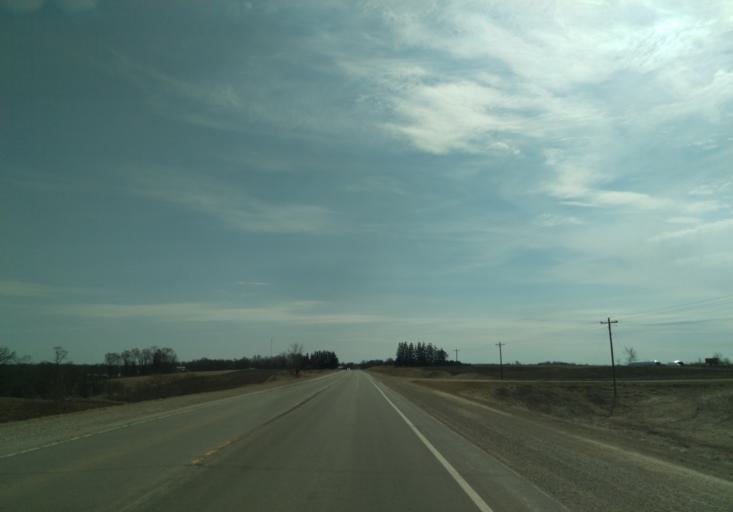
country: US
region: Iowa
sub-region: Winneshiek County
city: Decorah
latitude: 43.4384
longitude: -91.8612
